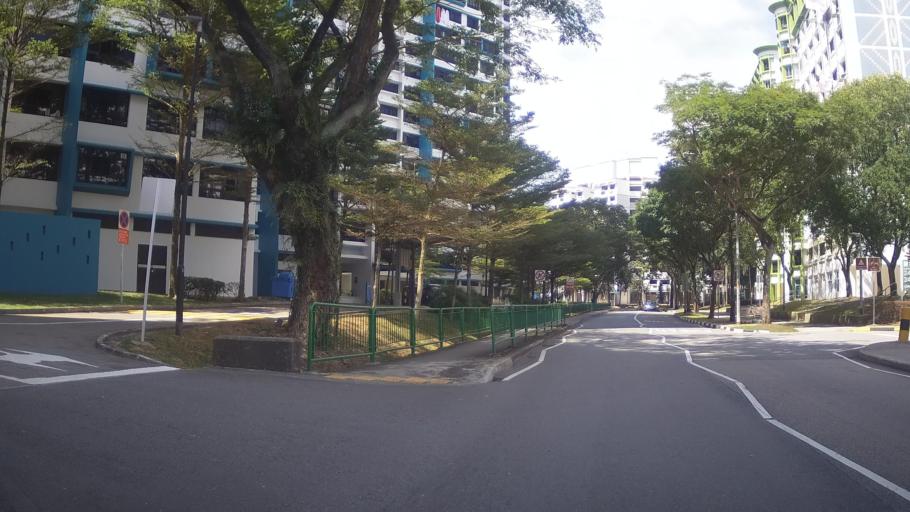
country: MY
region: Johor
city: Johor Bahru
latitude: 1.3396
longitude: 103.7221
